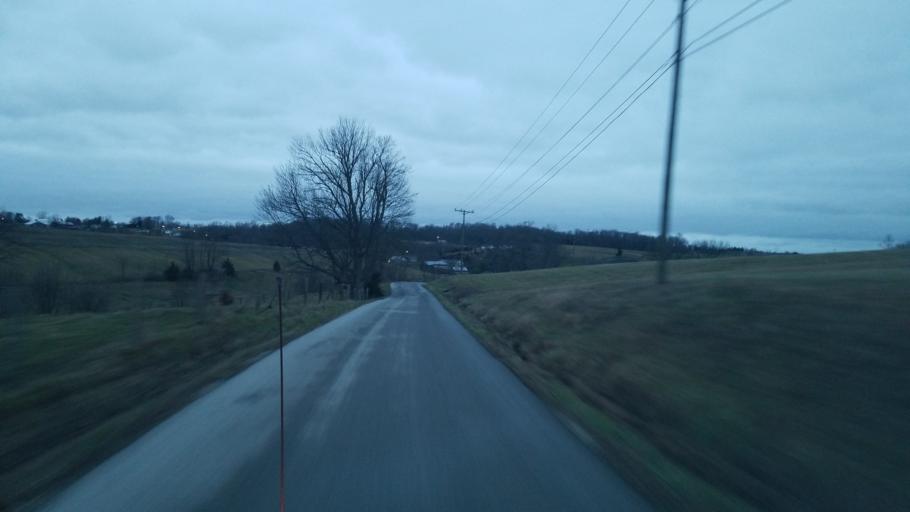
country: US
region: Kentucky
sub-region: Fleming County
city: Flemingsburg
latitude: 38.4946
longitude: -83.6620
